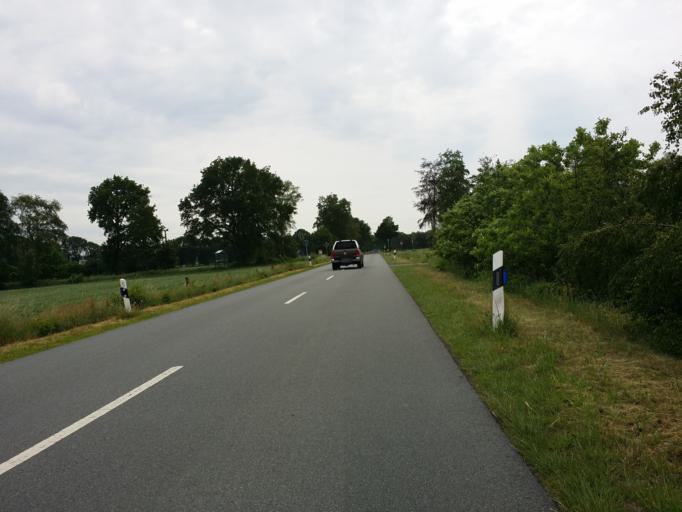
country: DE
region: Lower Saxony
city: Bockhorn
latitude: 53.3267
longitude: 8.0238
